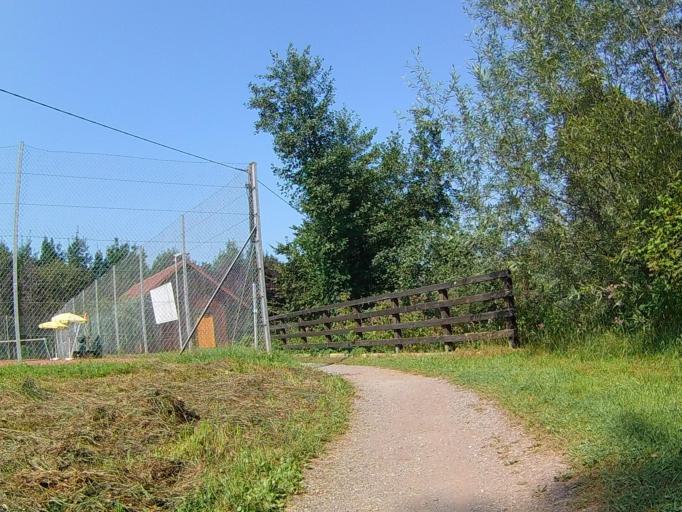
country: AT
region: Styria
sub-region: Politischer Bezirk Leibnitz
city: Leutschach
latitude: 46.6644
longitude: 15.4656
